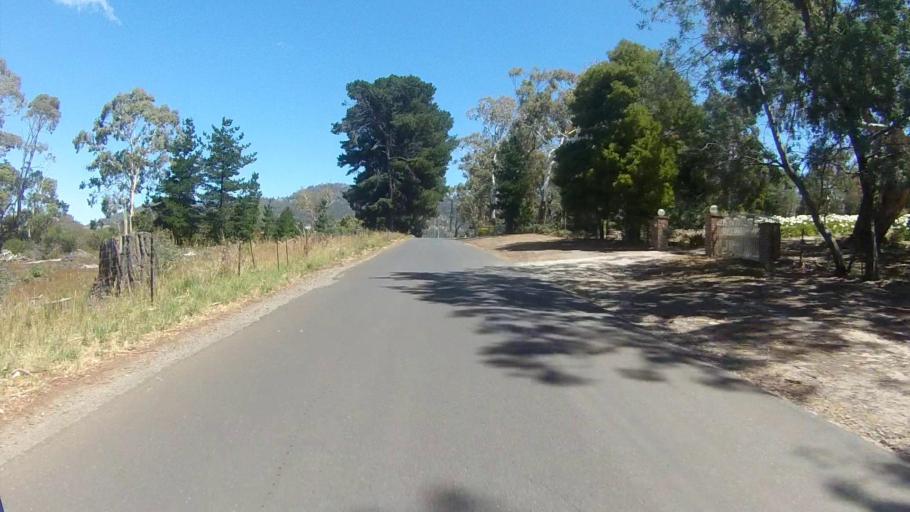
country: AU
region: Tasmania
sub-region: Clarence
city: Cambridge
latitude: -42.8389
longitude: 147.4634
